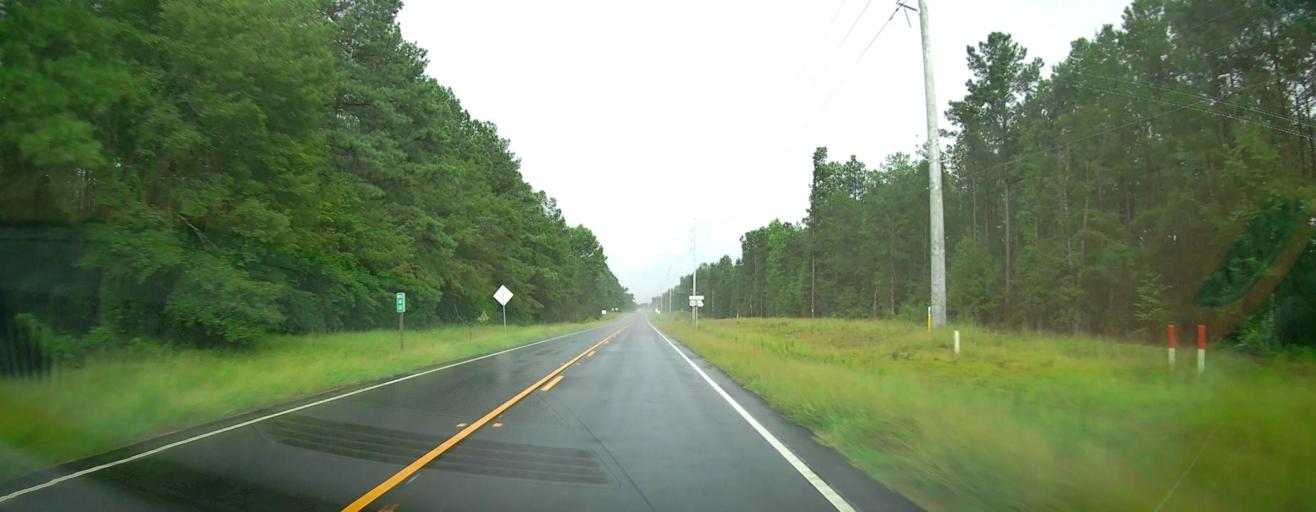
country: US
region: Georgia
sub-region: Twiggs County
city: Jeffersonville
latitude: 32.5827
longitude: -83.2174
